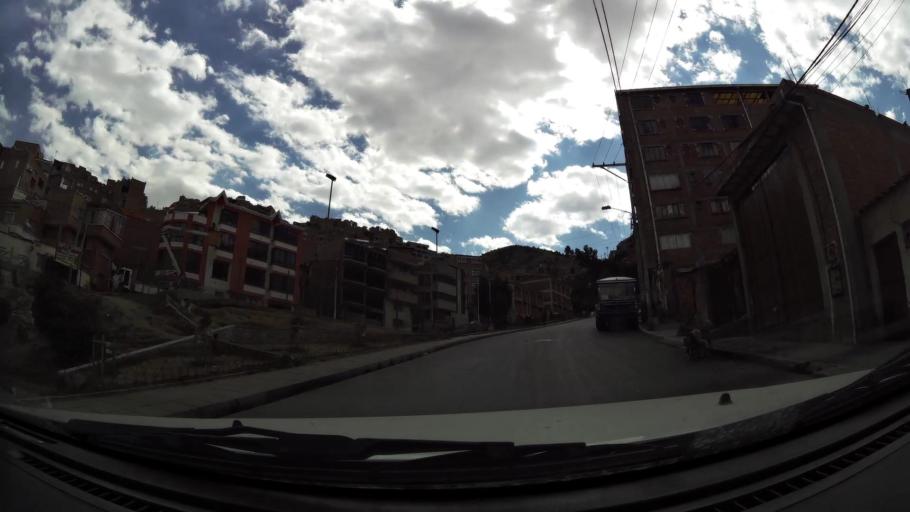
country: BO
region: La Paz
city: La Paz
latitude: -16.4764
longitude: -68.1242
